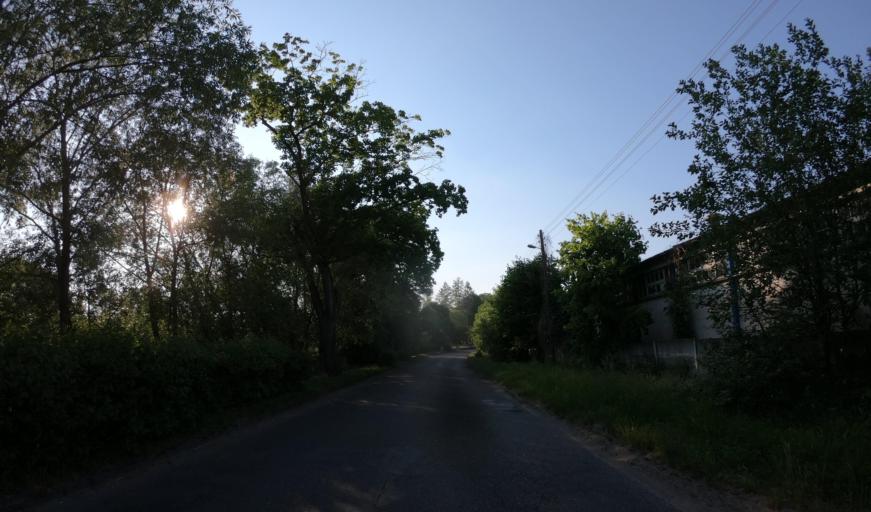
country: PL
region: West Pomeranian Voivodeship
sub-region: Powiat lobeski
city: Resko
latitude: 53.7655
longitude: 15.4045
